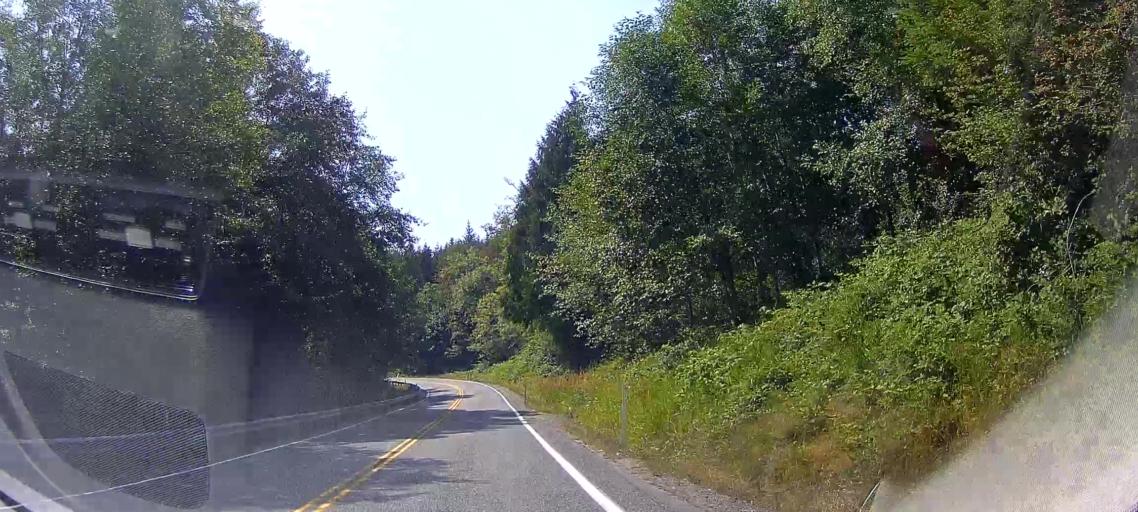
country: US
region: Washington
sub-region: Snohomish County
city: Bryant
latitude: 48.3395
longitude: -122.1184
